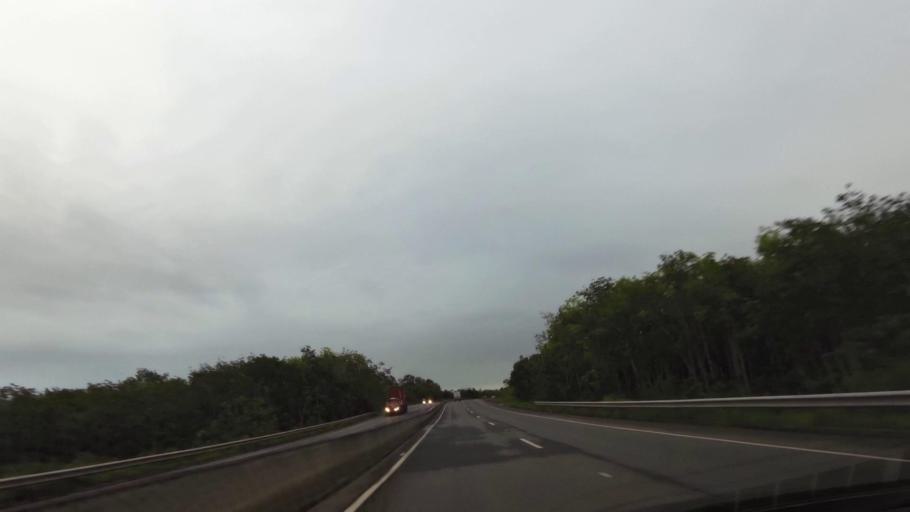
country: BR
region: Espirito Santo
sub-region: Guarapari
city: Guarapari
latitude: -20.6283
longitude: -40.5073
